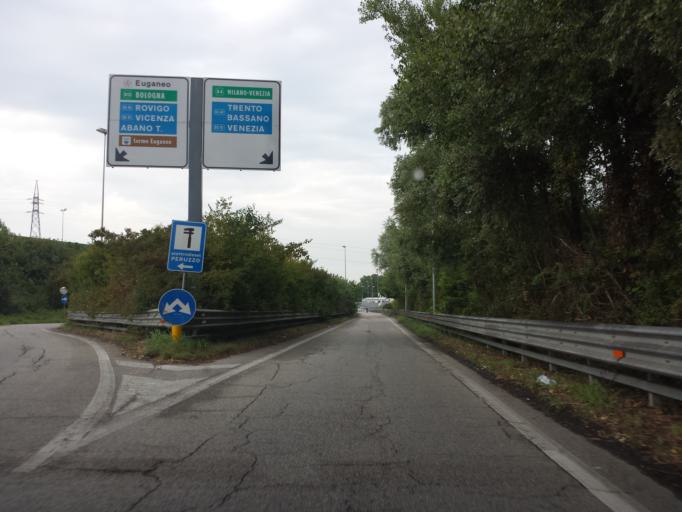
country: IT
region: Veneto
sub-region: Provincia di Padova
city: Vigodarzere
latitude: 45.4365
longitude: 11.8679
